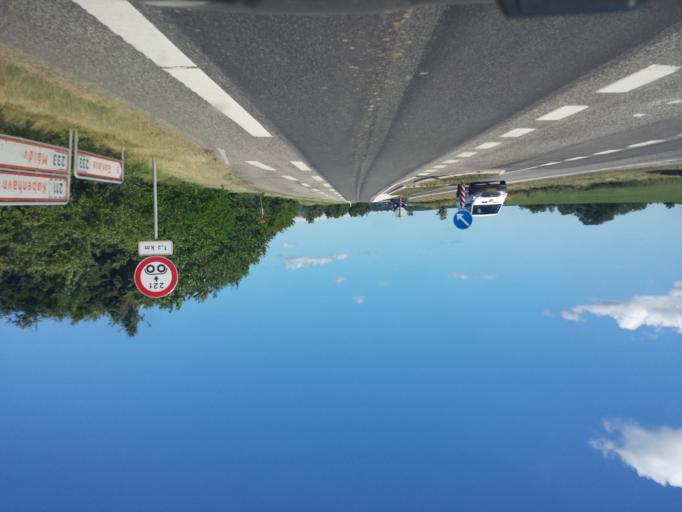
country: DK
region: Capital Region
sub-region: Egedal Kommune
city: Smorumnedre
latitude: 55.7629
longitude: 12.2940
